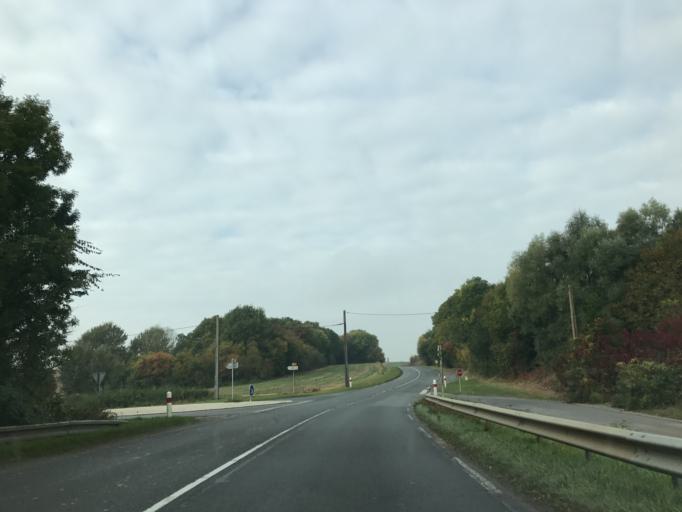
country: FR
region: Picardie
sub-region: Departement de la Somme
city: Peronne
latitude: 49.8764
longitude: 2.9193
